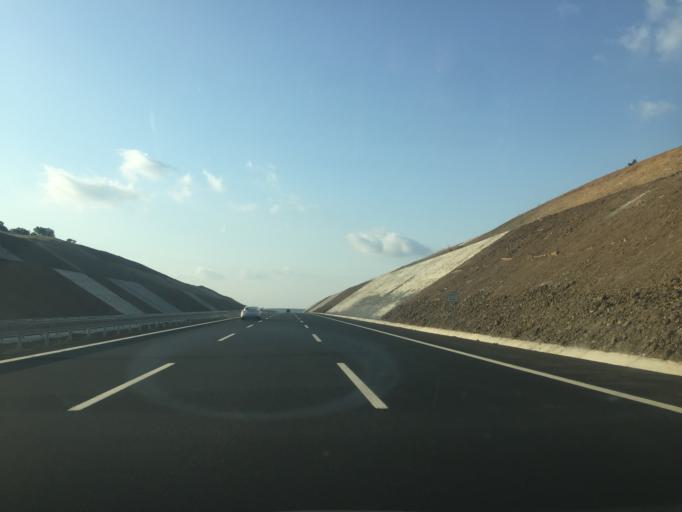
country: TR
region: Balikesir
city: Ertugrul
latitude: 39.5247
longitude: 27.6798
